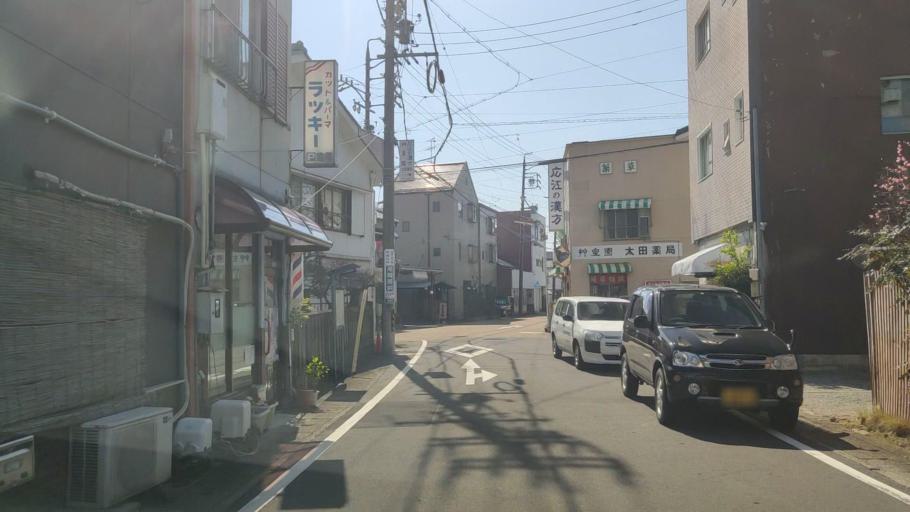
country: JP
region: Gifu
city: Gifu-shi
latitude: 35.4061
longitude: 136.7627
